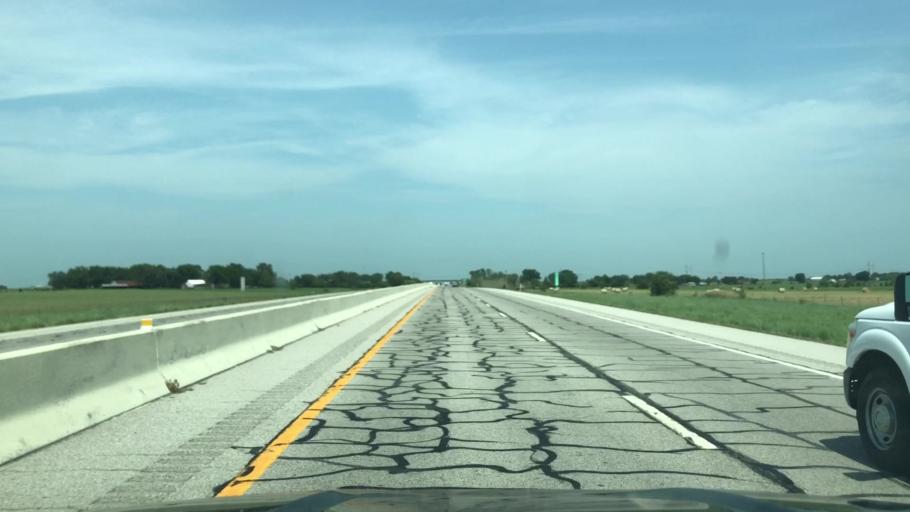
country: US
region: Oklahoma
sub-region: Craig County
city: Vinita
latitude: 36.5344
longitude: -95.2431
